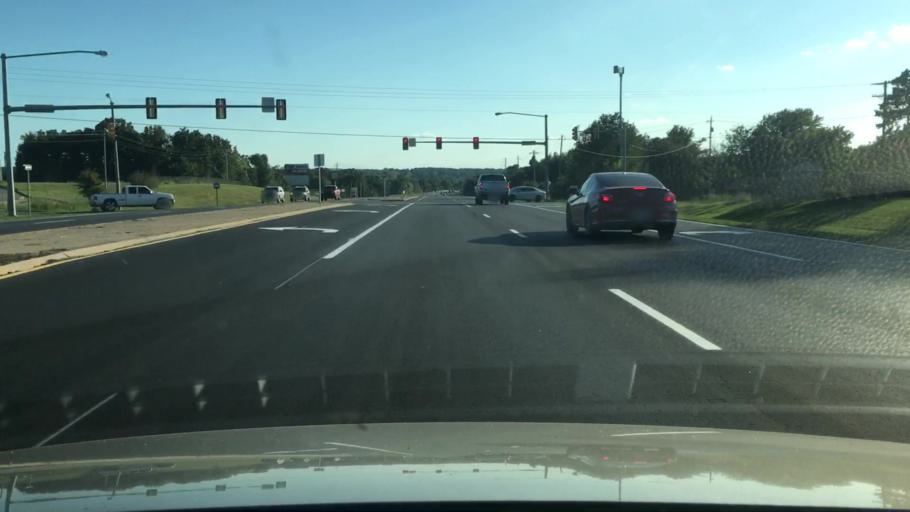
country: US
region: Oklahoma
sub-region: Cherokee County
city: Tahlequah
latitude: 35.9087
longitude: -94.9569
